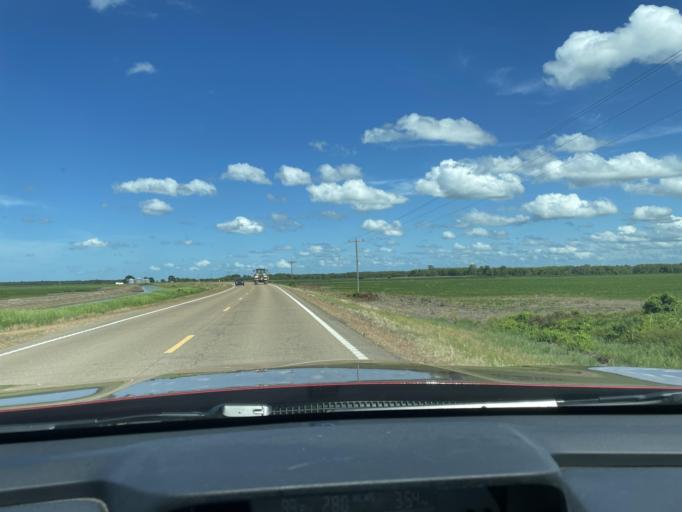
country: US
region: Mississippi
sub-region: Humphreys County
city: Belzoni
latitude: 33.1835
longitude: -90.6586
